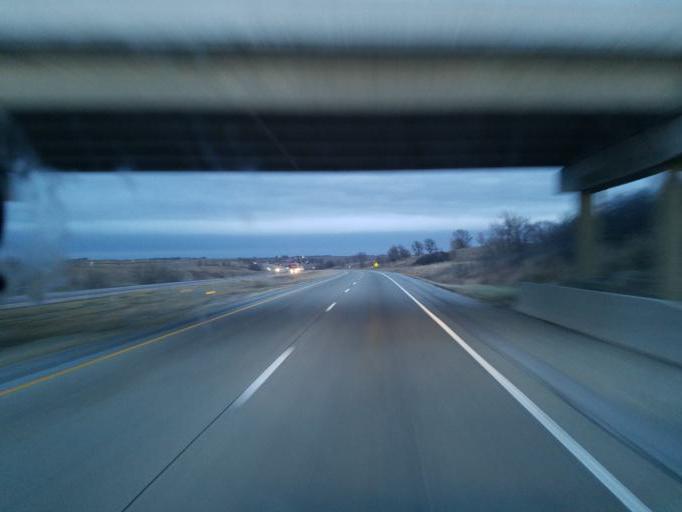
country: US
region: Iowa
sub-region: Cass County
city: Atlantic
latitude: 41.4971
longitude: -95.1182
